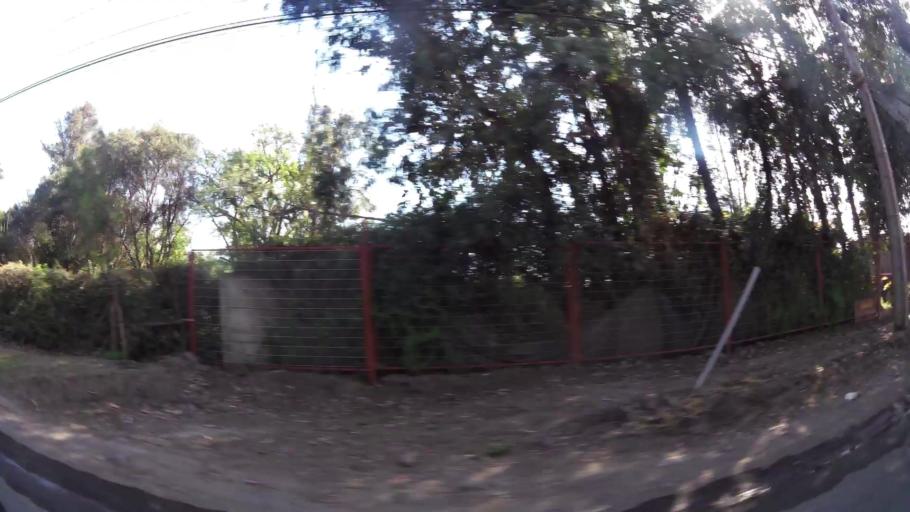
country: CL
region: Santiago Metropolitan
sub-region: Provincia de Talagante
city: Penaflor
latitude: -33.5525
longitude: -70.8378
